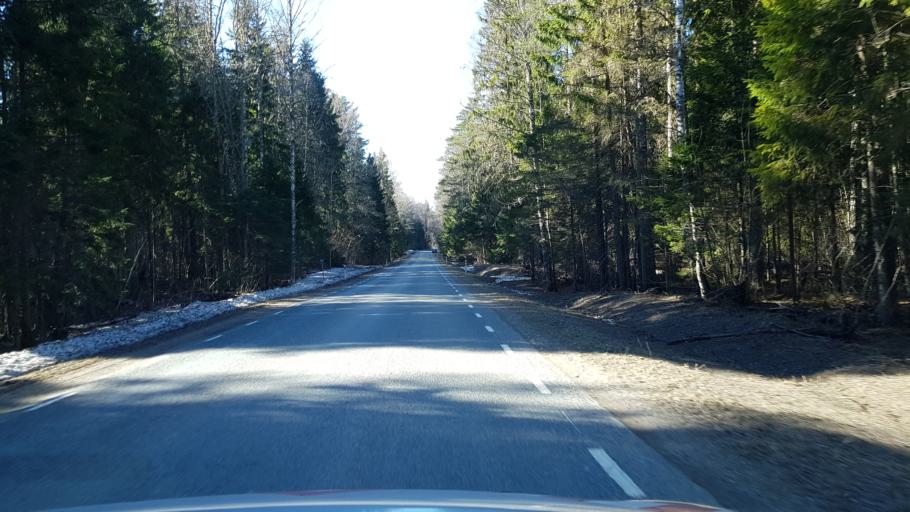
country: EE
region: Laeaene-Virumaa
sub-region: Vinni vald
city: Vinni
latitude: 59.2671
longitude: 26.6697
